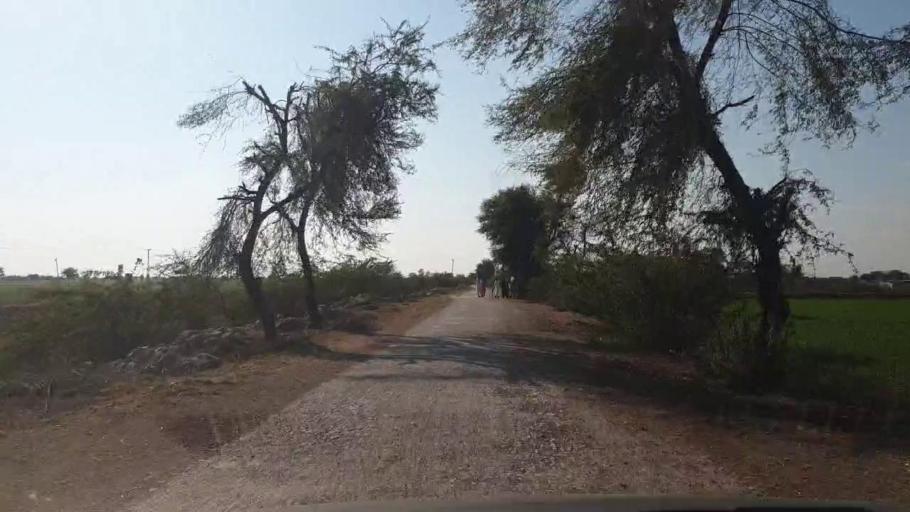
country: PK
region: Sindh
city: Shahpur Chakar
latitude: 26.1669
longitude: 68.6830
